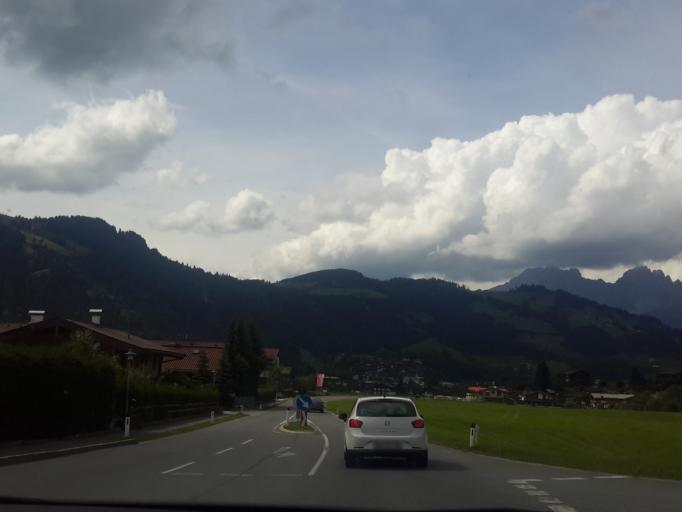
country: AT
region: Tyrol
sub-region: Politischer Bezirk Kitzbuhel
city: Reith bei Kitzbuhel
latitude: 47.4656
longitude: 12.3520
